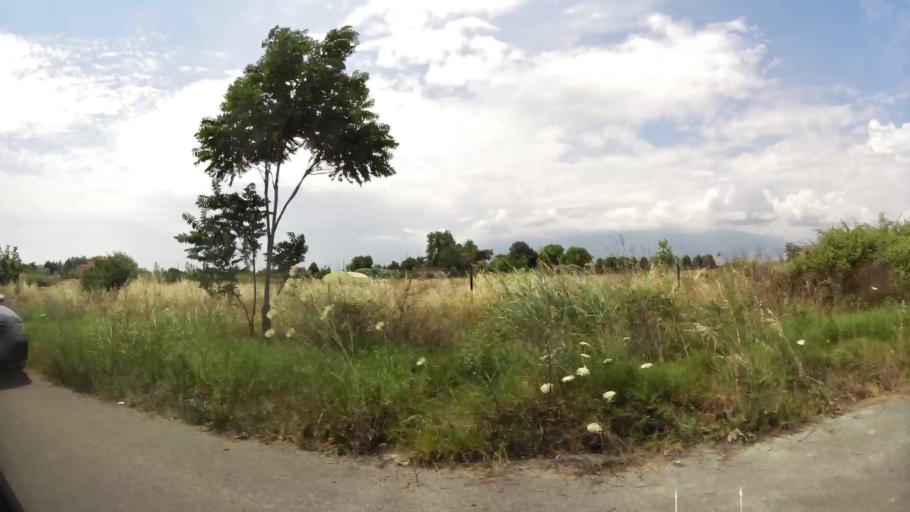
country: GR
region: Central Macedonia
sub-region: Nomos Pierias
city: Katerini
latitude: 40.2614
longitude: 22.5179
